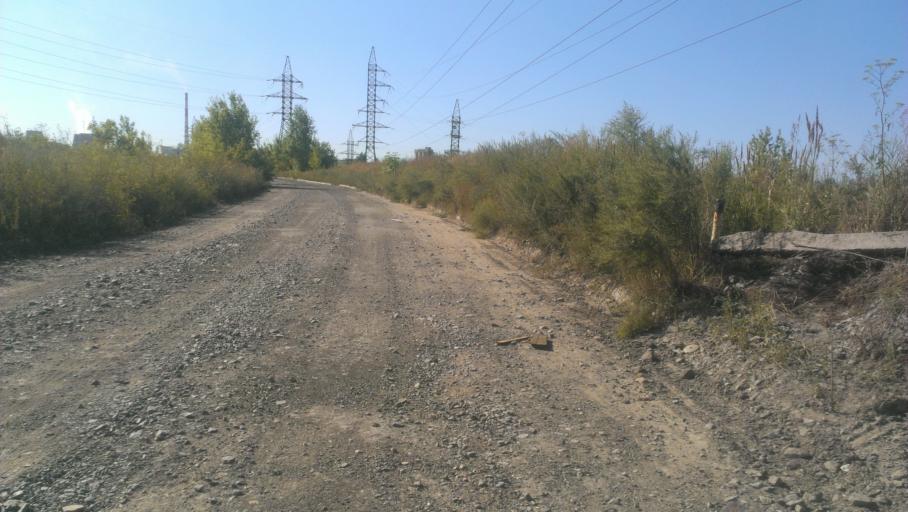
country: RU
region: Altai Krai
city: Novosilikatnyy
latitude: 53.3271
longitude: 83.6468
